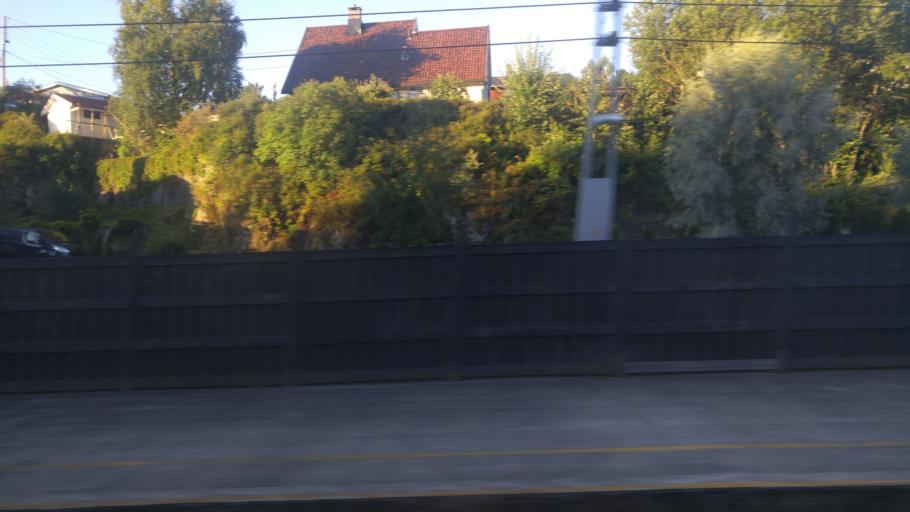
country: NO
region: Akershus
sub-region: Lorenskog
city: Kjenn
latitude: 59.9479
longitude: 10.9291
